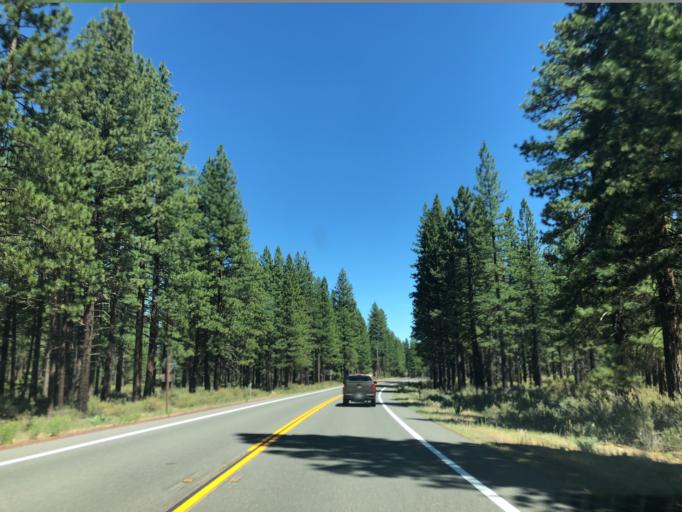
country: US
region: California
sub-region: Lassen County
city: Susanville
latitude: 40.4157
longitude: -120.7641
